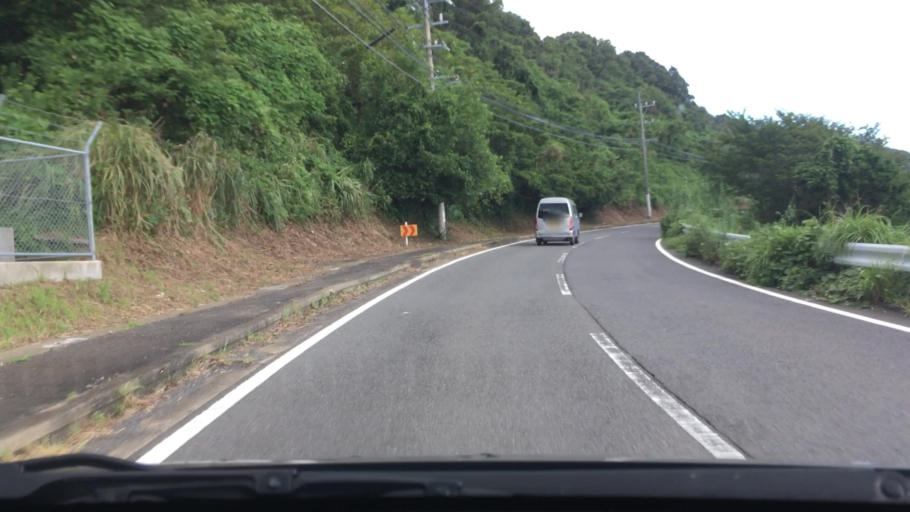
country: JP
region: Nagasaki
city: Togitsu
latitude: 32.8683
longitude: 129.6803
